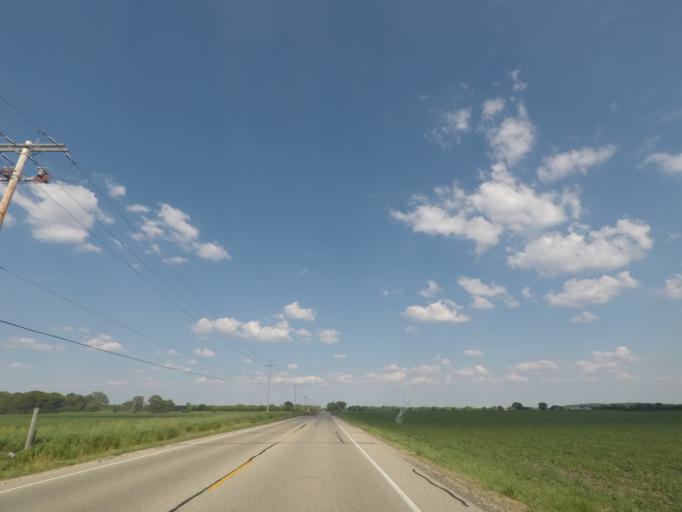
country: US
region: Wisconsin
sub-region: Walworth County
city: East Troy
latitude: 42.7927
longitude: -88.4439
